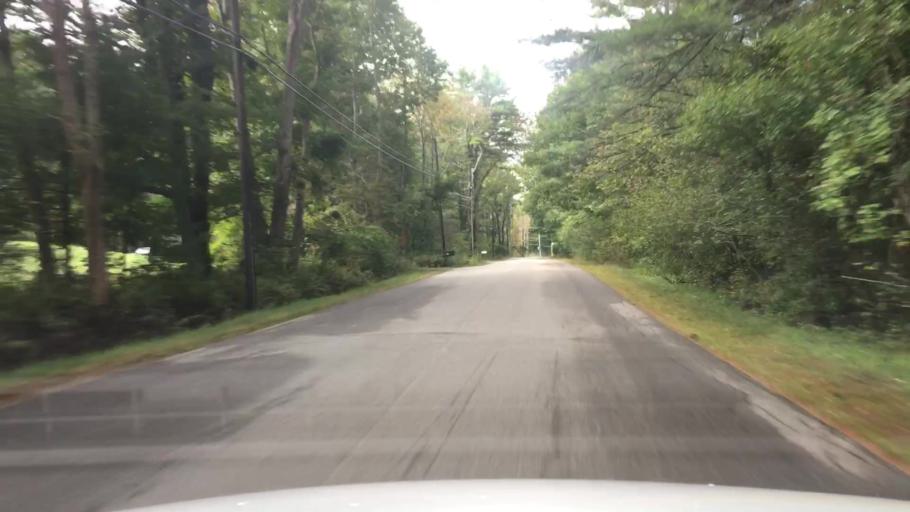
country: US
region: Maine
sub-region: York County
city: Kittery Point
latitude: 43.0999
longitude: -70.7017
